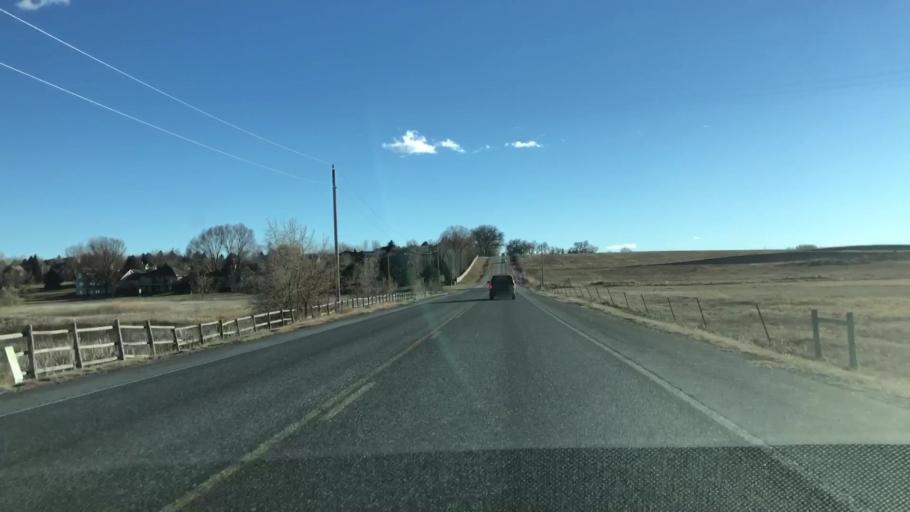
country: US
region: Colorado
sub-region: Weld County
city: Windsor
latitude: 40.4883
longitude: -104.9820
